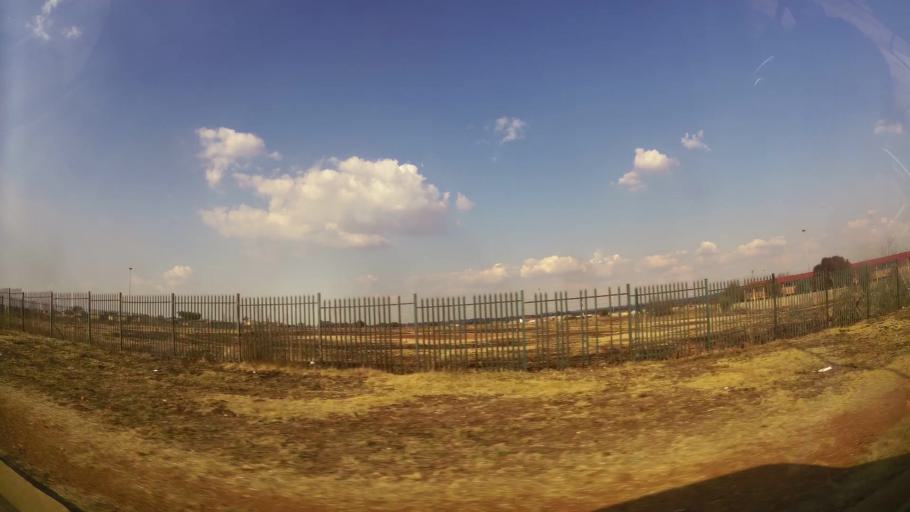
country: ZA
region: Gauteng
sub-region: Ekurhuleni Metropolitan Municipality
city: Germiston
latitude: -26.3683
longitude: 28.2190
